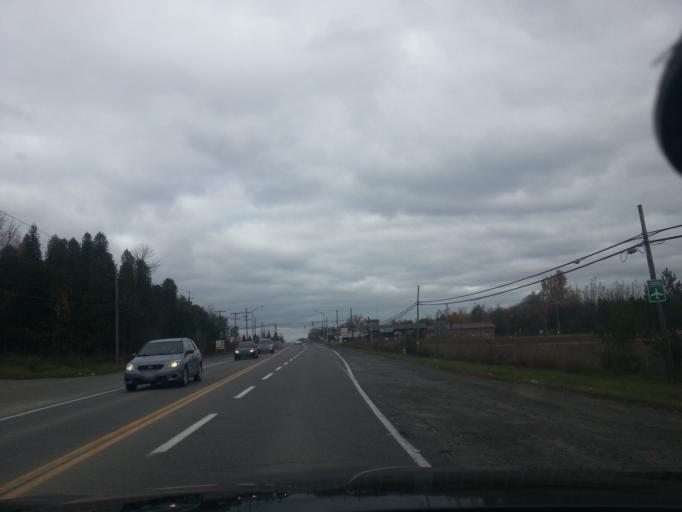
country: CA
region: Ontario
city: Ottawa
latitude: 45.2953
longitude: -75.5791
